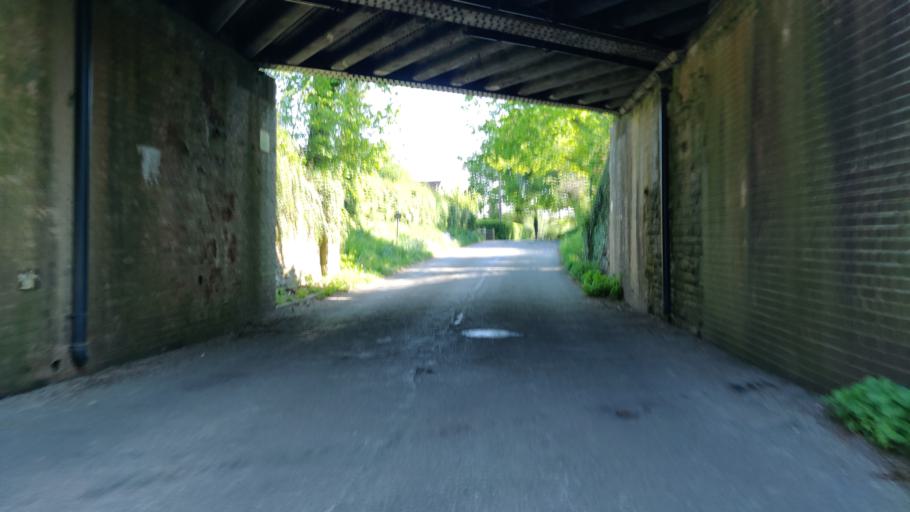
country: GB
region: England
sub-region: West Sussex
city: Southwater
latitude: 51.0308
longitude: -0.3904
